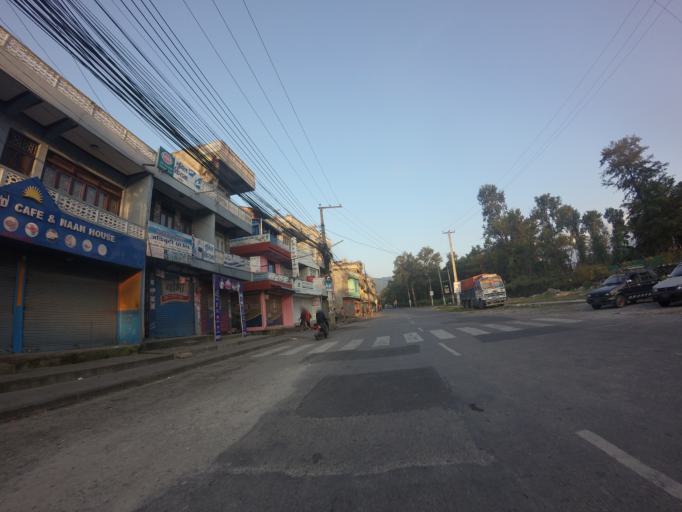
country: NP
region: Western Region
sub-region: Gandaki Zone
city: Pokhara
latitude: 28.2217
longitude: 83.9949
